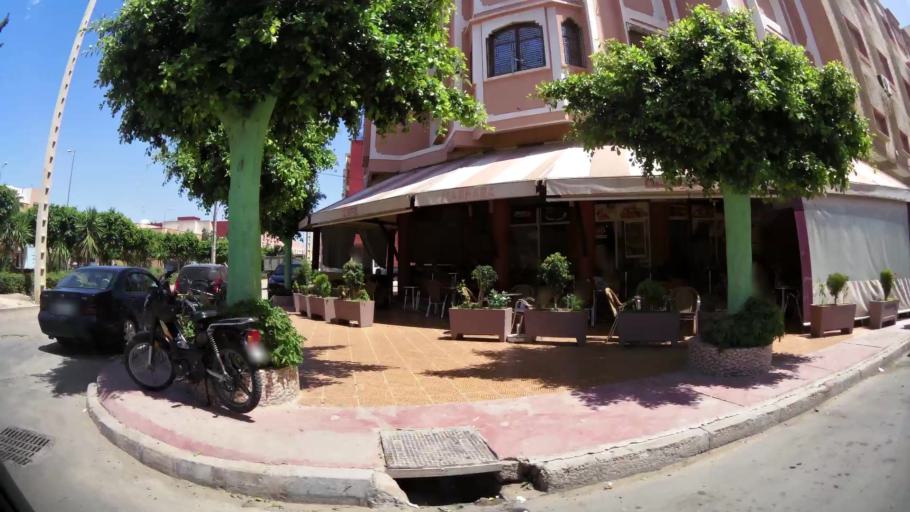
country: MA
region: Souss-Massa-Draa
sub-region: Inezgane-Ait Mellou
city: Inezgane
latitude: 30.3380
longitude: -9.5037
